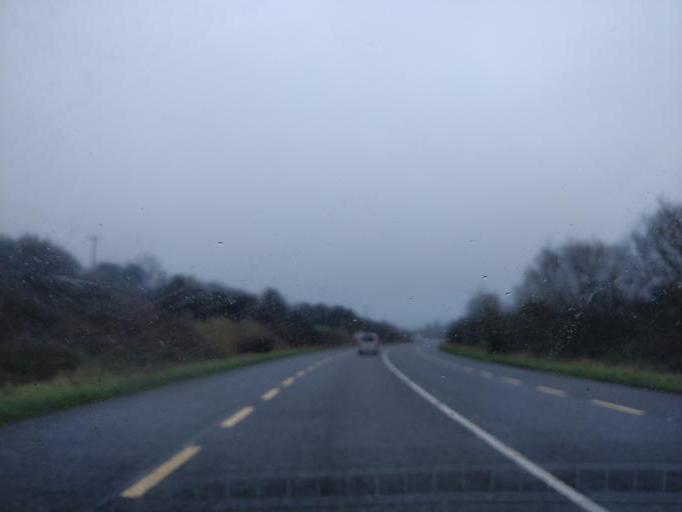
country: IE
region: Connaught
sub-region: Maigh Eo
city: Foxford
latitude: 53.8940
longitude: -9.1825
